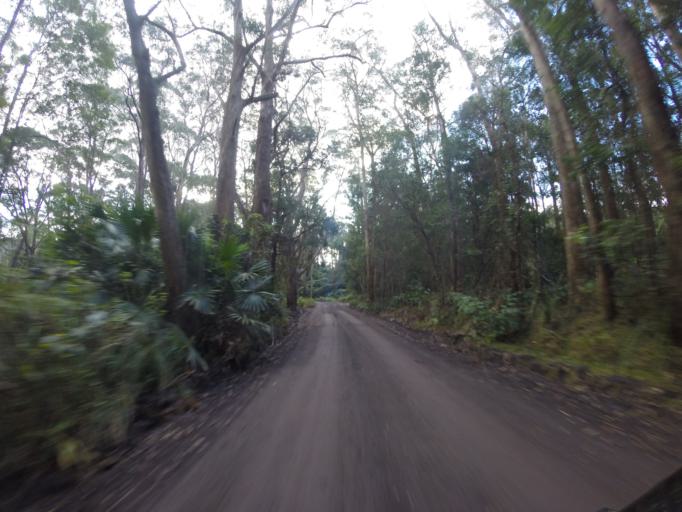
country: AU
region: New South Wales
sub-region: Wollongong
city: Cordeaux Heights
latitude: -34.4288
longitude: 150.7825
